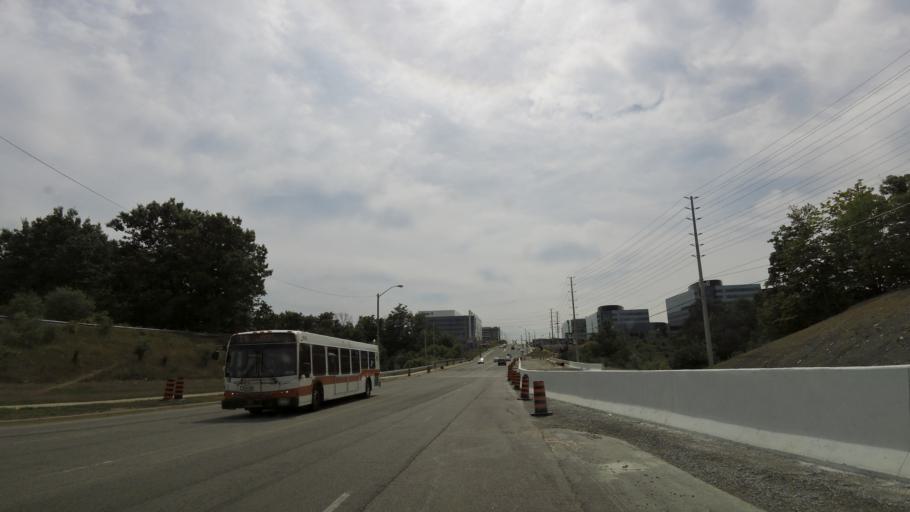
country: CA
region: Ontario
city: Etobicoke
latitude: 43.6474
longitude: -79.6077
